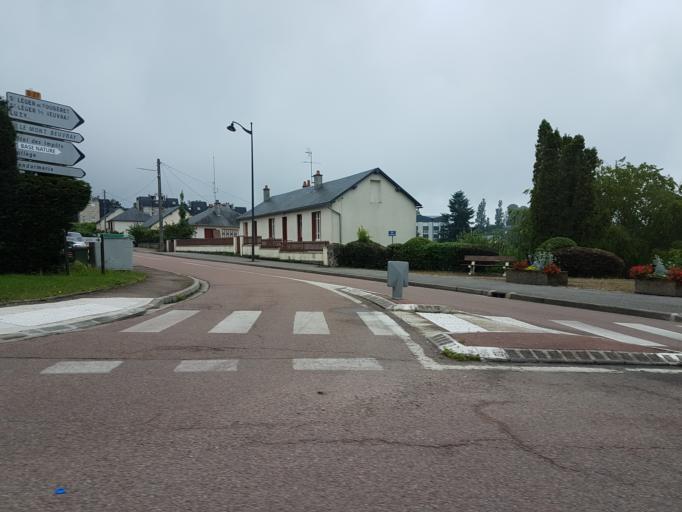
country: FR
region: Bourgogne
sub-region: Departement de la Nievre
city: Chateau-Chinon(Ville)
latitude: 47.0589
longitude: 3.9355
